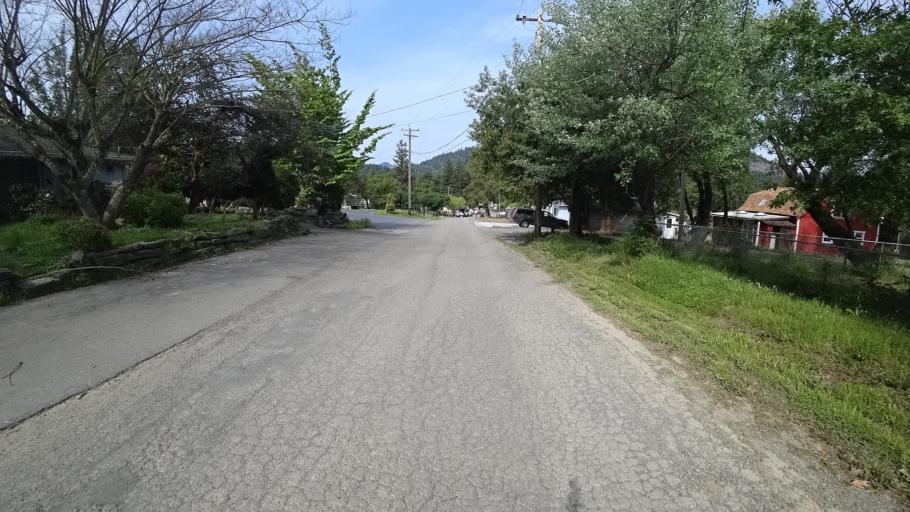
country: US
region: California
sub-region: Humboldt County
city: Redway
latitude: 40.2358
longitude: -123.8204
